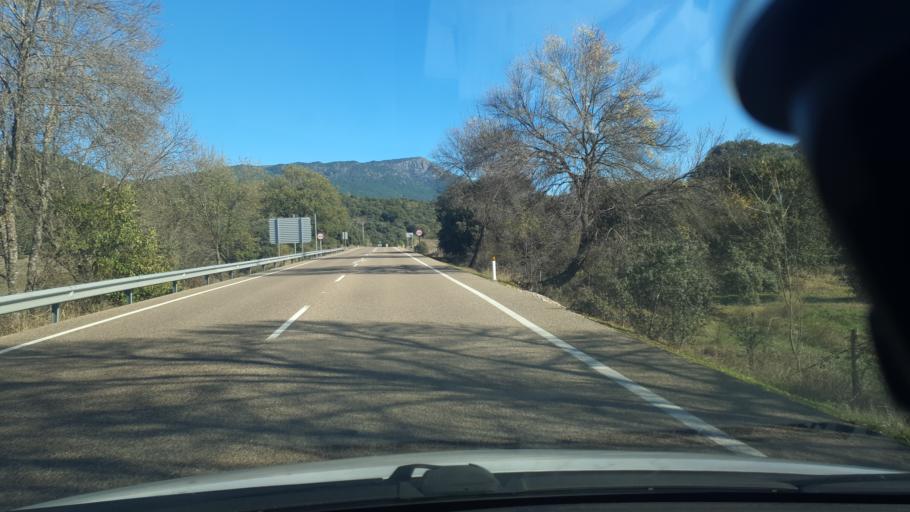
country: ES
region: Castille and Leon
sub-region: Provincia de Avila
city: Arenas de San Pedro
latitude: 40.1815
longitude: -5.0376
